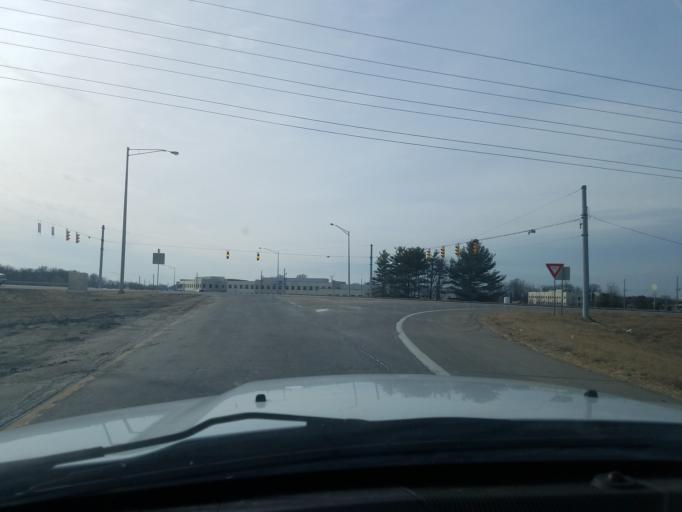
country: US
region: Indiana
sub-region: Hancock County
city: Greenfield
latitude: 39.8220
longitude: -85.7692
